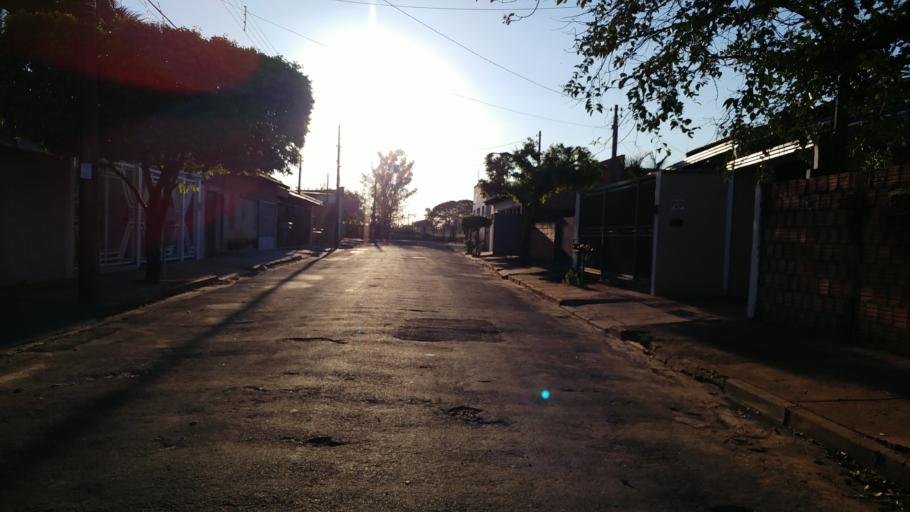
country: BR
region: Sao Paulo
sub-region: Paraguacu Paulista
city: Paraguacu Paulista
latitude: -22.4321
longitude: -50.5839
